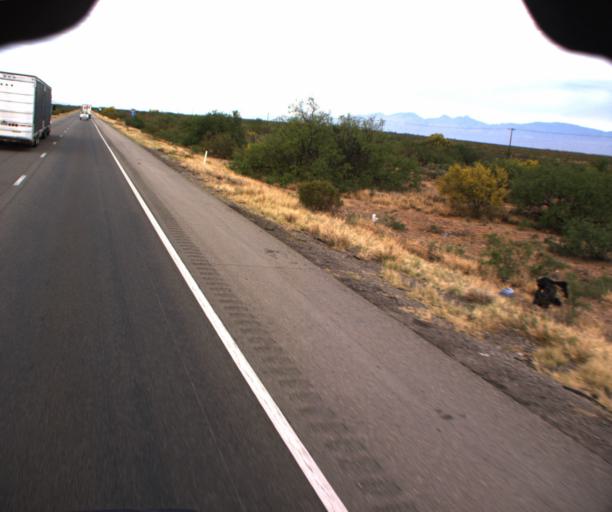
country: US
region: Arizona
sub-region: Pima County
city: Vail
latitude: 32.0335
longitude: -110.7275
